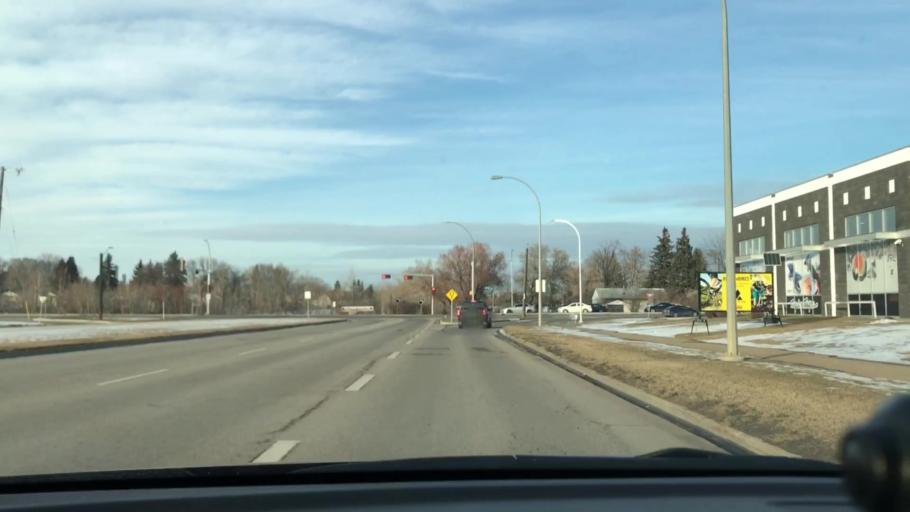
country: CA
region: Alberta
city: Edmonton
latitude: 53.4989
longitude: -113.4670
